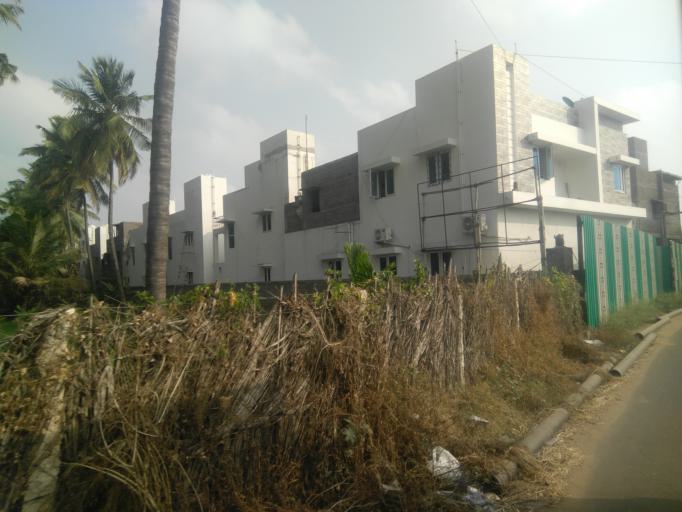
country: IN
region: Tamil Nadu
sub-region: Coimbatore
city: Periyanayakkanpalaiyam
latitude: 11.0769
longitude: 76.9218
